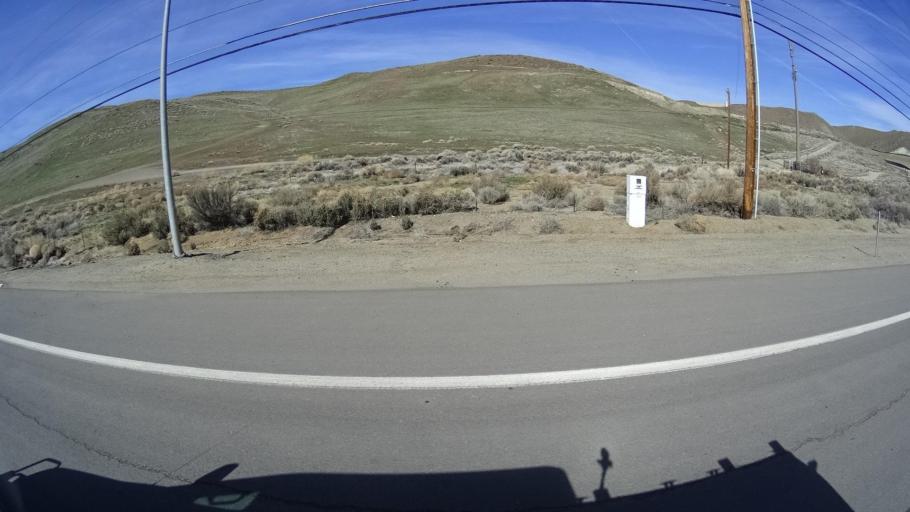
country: US
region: Nevada
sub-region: Washoe County
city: Sun Valley
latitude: 39.6067
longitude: -119.7331
